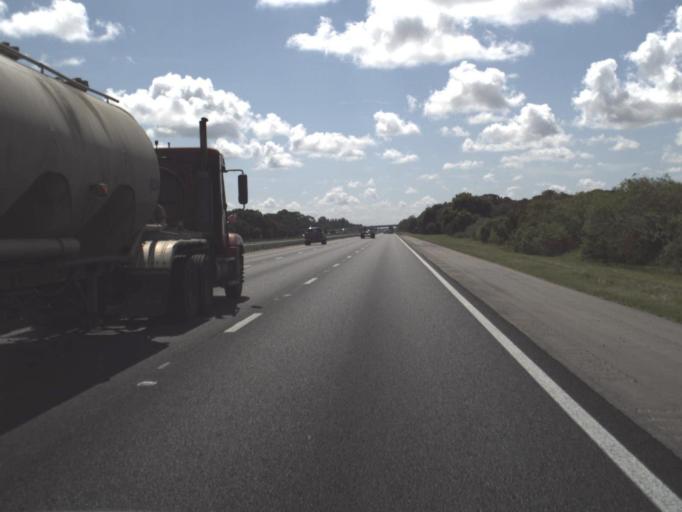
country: US
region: Florida
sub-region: Lee County
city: Suncoast Estates
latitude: 26.7479
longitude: -81.8603
